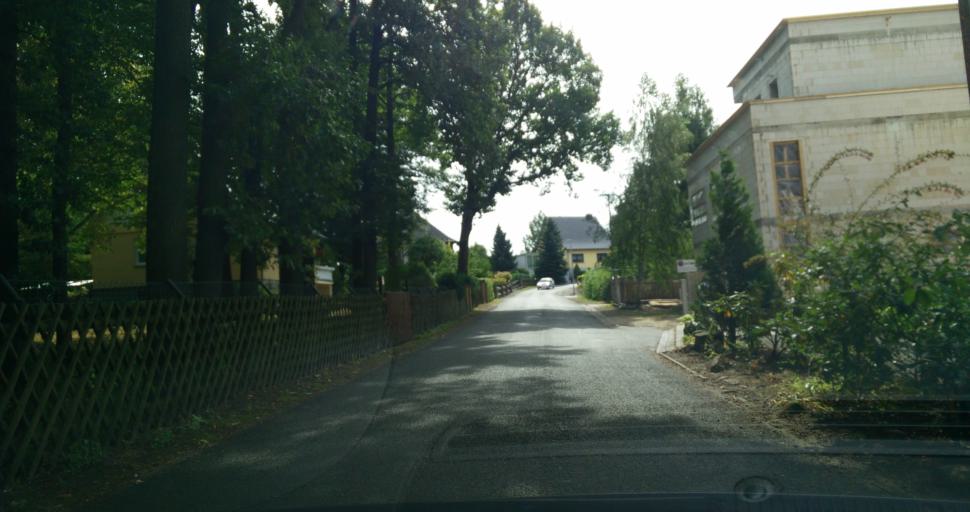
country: DE
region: Saxony
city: Bad Lausick
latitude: 51.1471
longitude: 12.6733
